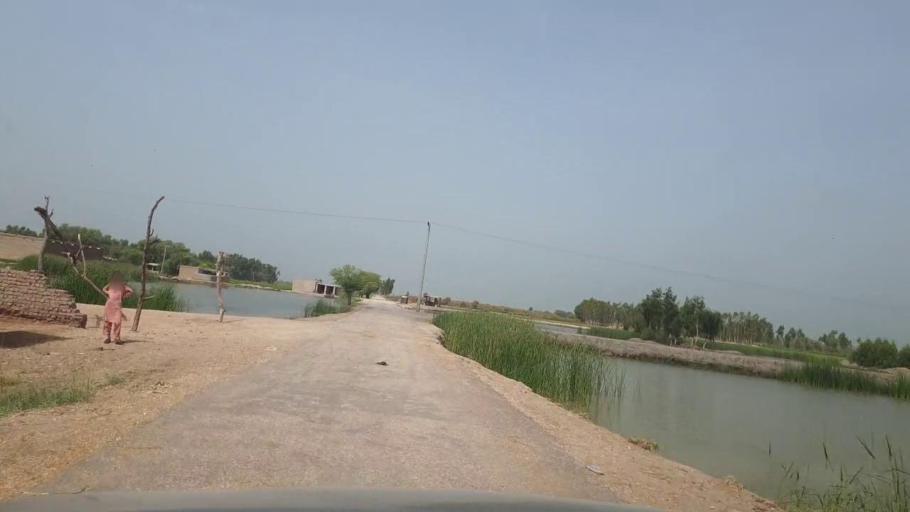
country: PK
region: Sindh
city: Garhi Yasin
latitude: 27.9191
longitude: 68.4373
